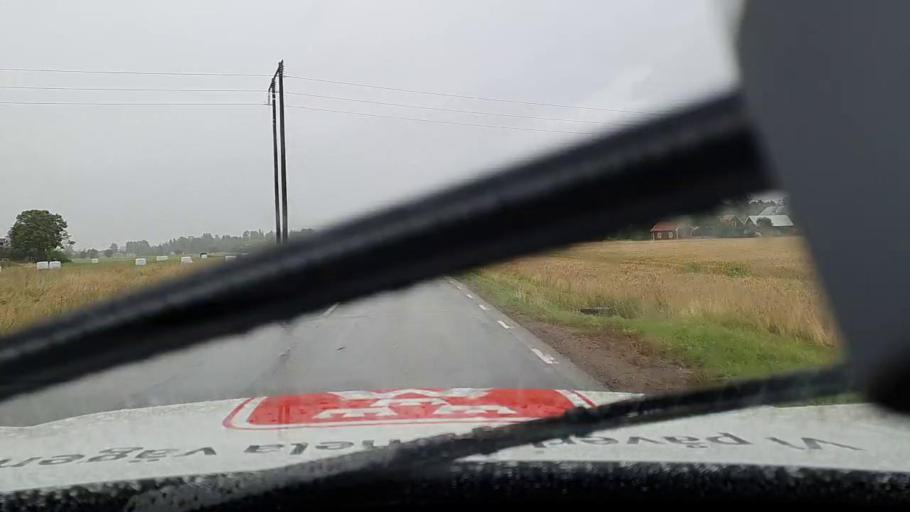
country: SE
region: Vaestra Goetaland
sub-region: Toreboda Kommun
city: Toereboda
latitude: 58.6935
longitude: 14.1304
